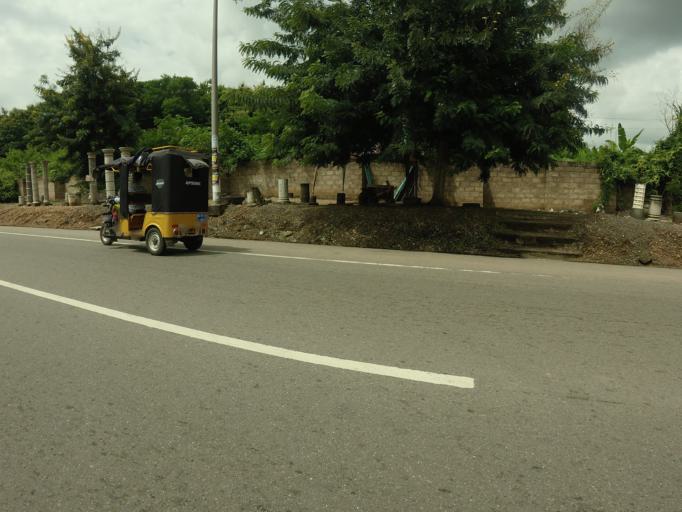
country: GH
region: Volta
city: Ho
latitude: 6.5935
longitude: 0.4720
